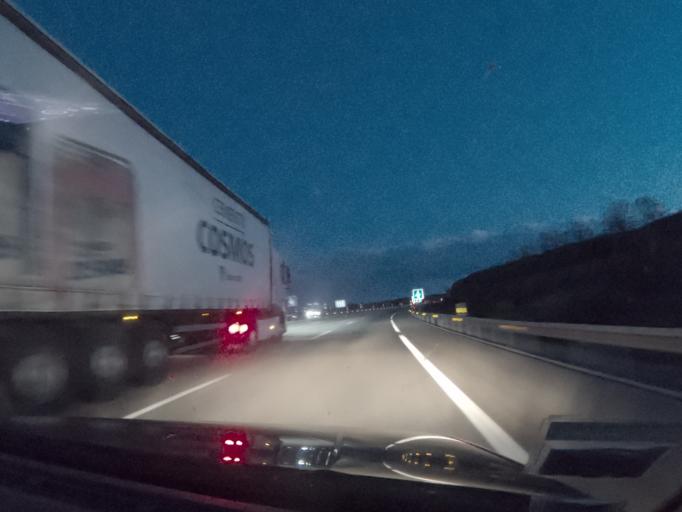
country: ES
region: Castille and Leon
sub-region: Provincia de Leon
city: Villagaton
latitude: 42.5888
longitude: -6.2157
